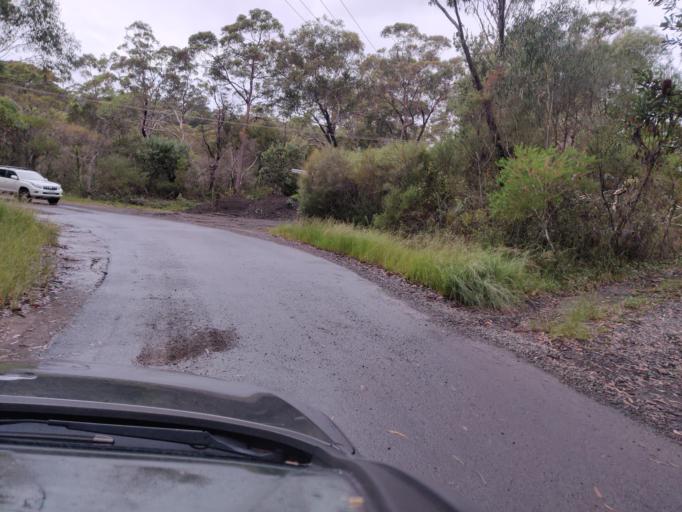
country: AU
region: New South Wales
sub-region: Pittwater
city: Ingleside
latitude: -33.6807
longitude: 151.2533
